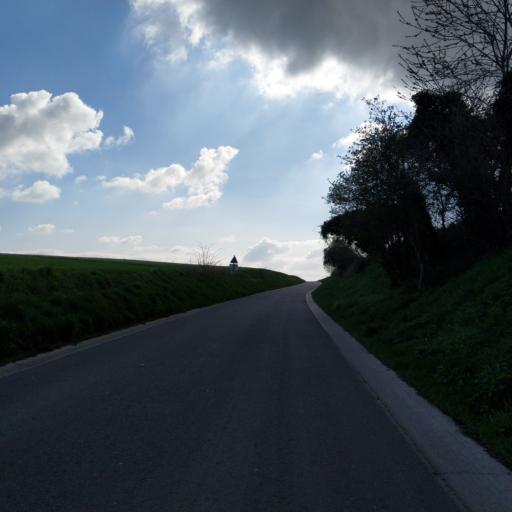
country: BE
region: Wallonia
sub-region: Province du Hainaut
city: Lens
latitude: 50.5892
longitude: 3.9000
